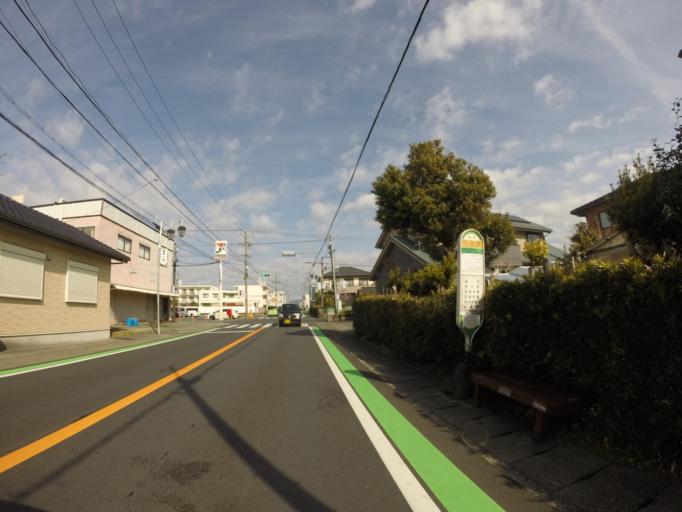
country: JP
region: Shizuoka
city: Hamakita
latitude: 34.7836
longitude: 137.7081
